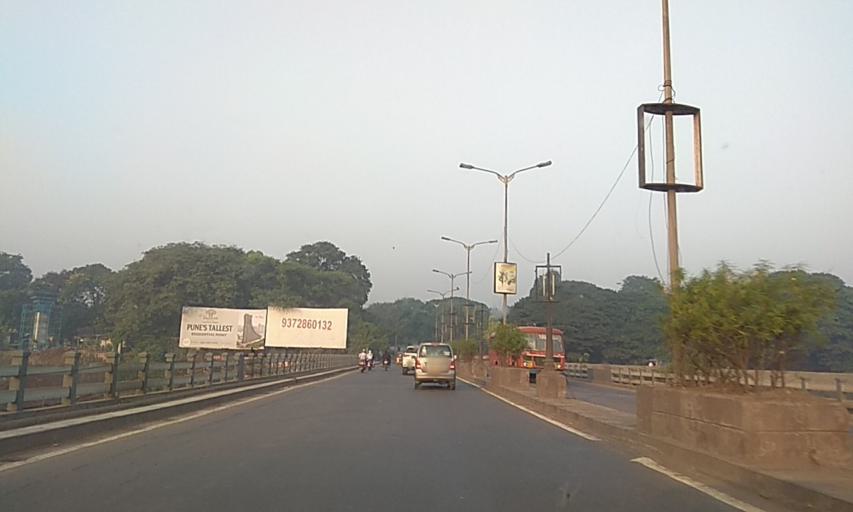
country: IN
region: Maharashtra
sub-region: Pune Division
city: Shivaji Nagar
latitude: 18.5297
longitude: 73.8606
